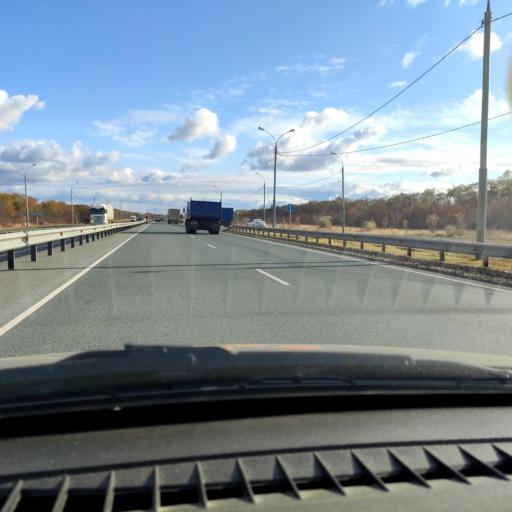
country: RU
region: Samara
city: Varlamovo
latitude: 53.1961
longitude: 48.2956
